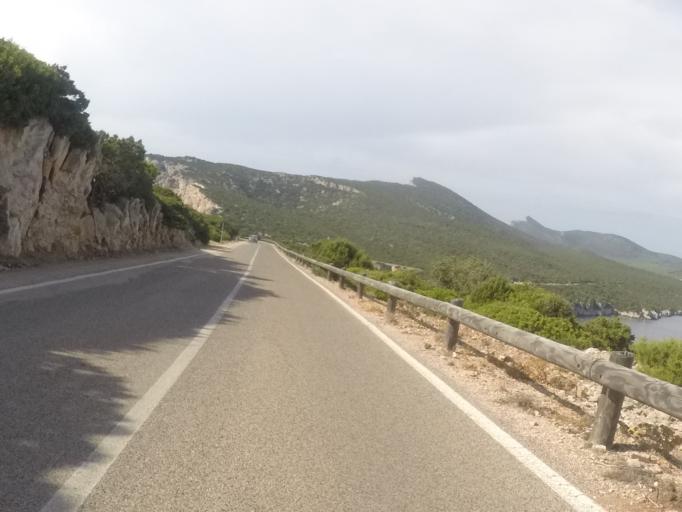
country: IT
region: Sardinia
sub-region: Provincia di Sassari
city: Alghero
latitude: 40.5720
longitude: 8.1630
